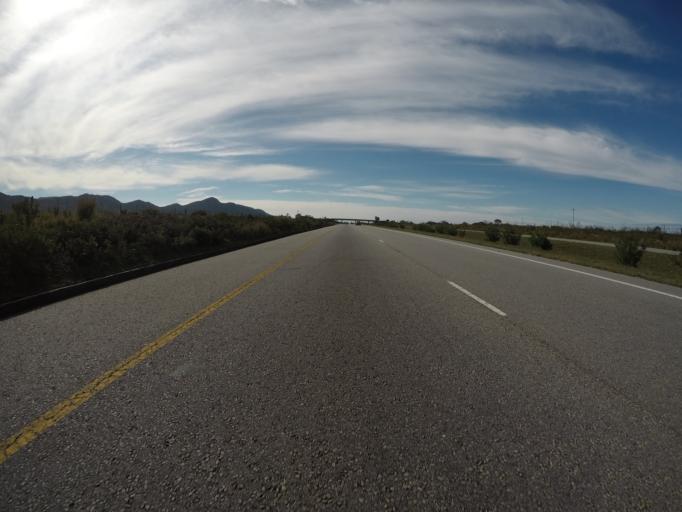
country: ZA
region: Eastern Cape
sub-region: Nelson Mandela Bay Metropolitan Municipality
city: Uitenhage
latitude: -33.9100
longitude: 25.2145
